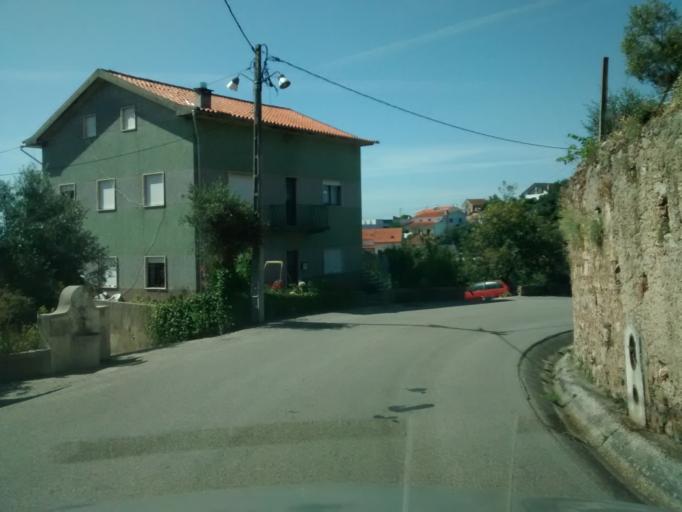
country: PT
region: Aveiro
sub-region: Mealhada
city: Pampilhosa do Botao
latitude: 40.3840
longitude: -8.3830
